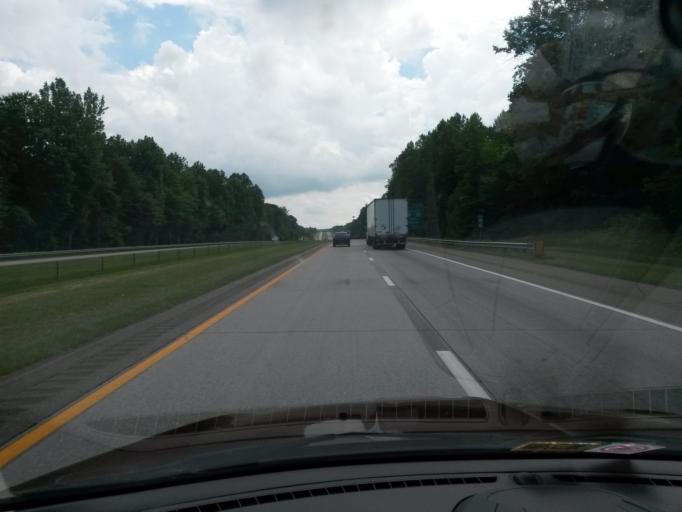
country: US
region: North Carolina
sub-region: Surry County
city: Elkin
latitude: 36.2985
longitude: -80.8112
